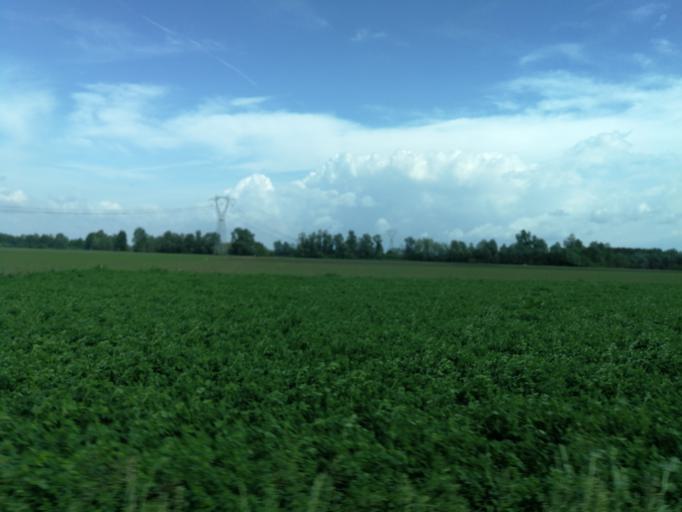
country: IT
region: Piedmont
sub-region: Provincia di Torino
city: Pancalieri
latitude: 44.8199
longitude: 7.5860
